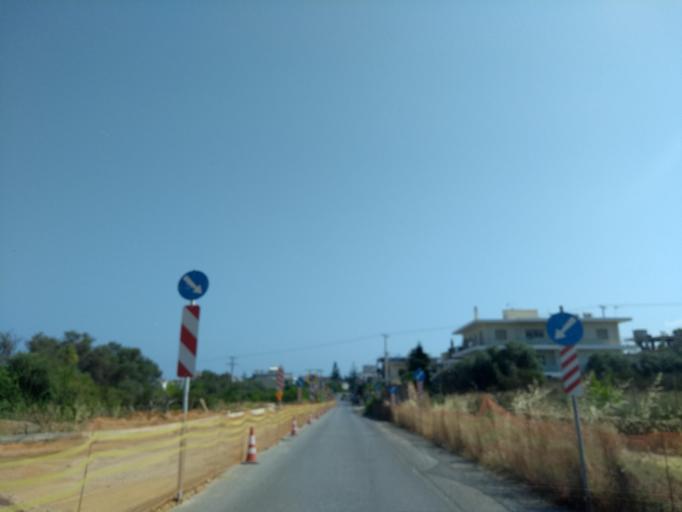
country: GR
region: Crete
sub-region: Nomos Chanias
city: Chania
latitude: 35.4997
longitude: 24.0187
